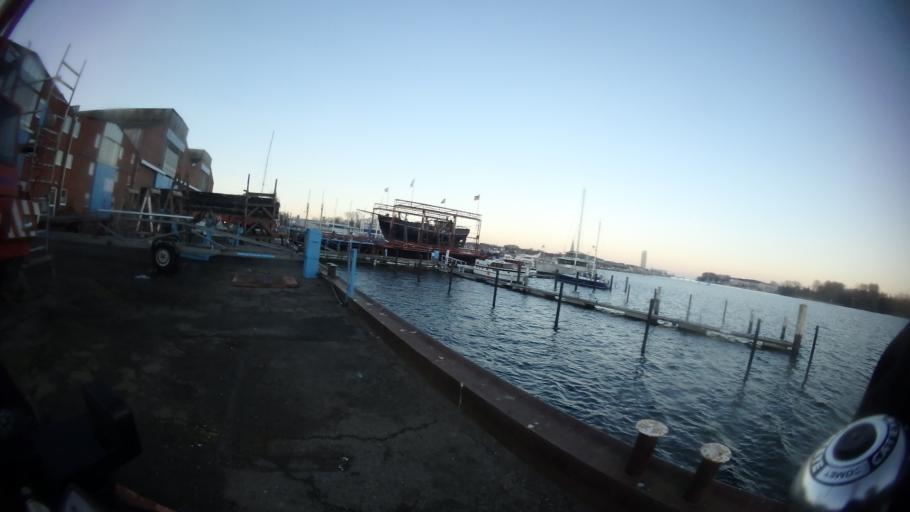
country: DE
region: Schleswig-Holstein
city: Travemuende
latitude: 53.9517
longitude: 10.8572
